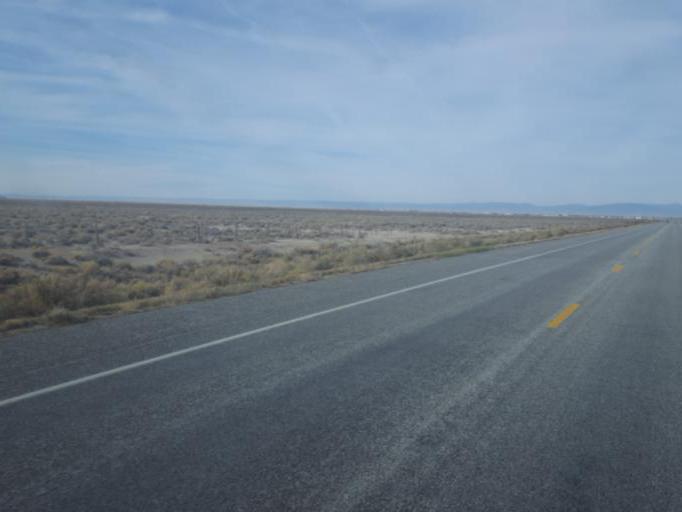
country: US
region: Colorado
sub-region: Alamosa County
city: Alamosa East
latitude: 37.4749
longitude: -105.6485
